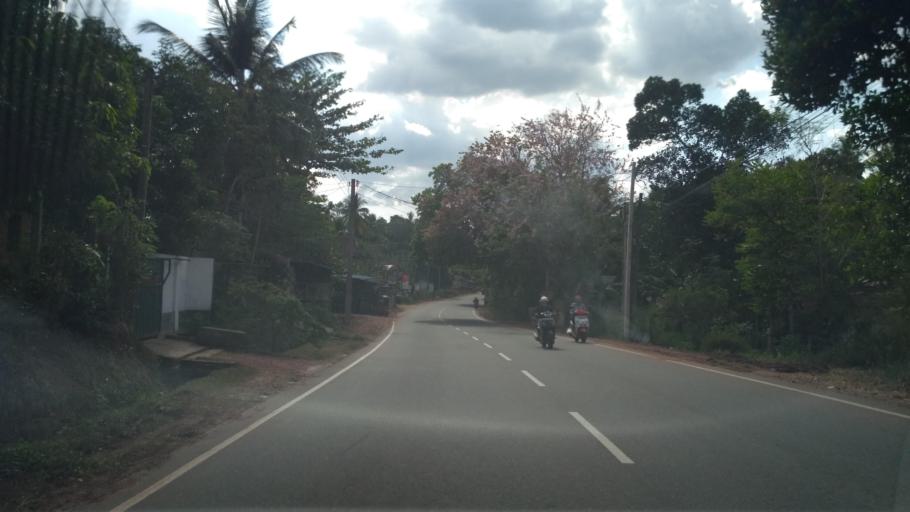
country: LK
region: North Western
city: Kuliyapitiya
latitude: 7.3255
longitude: 80.0432
